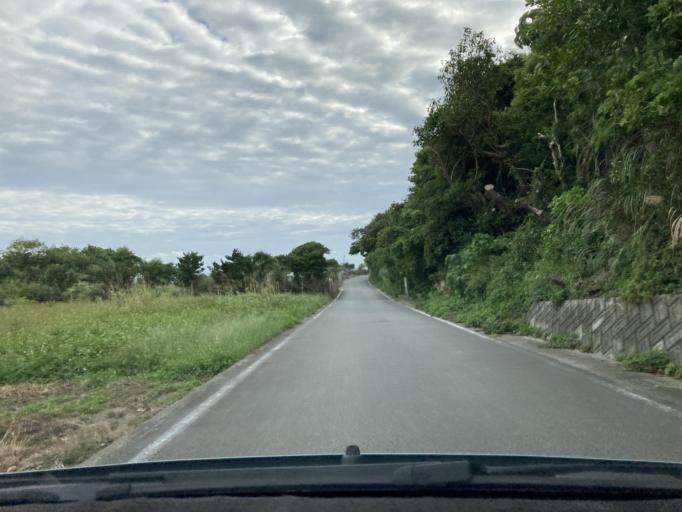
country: JP
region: Okinawa
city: Tomigusuku
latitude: 26.1367
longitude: 127.7929
